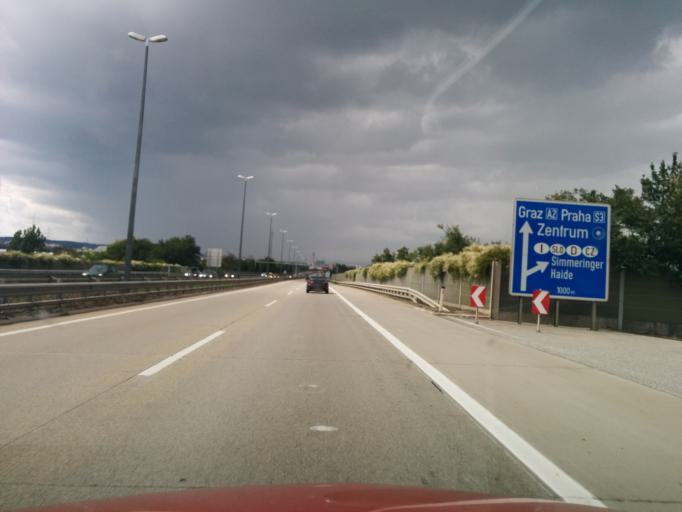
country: AT
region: Lower Austria
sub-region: Politischer Bezirk Wien-Umgebung
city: Schwechat
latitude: 48.1650
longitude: 16.4709
